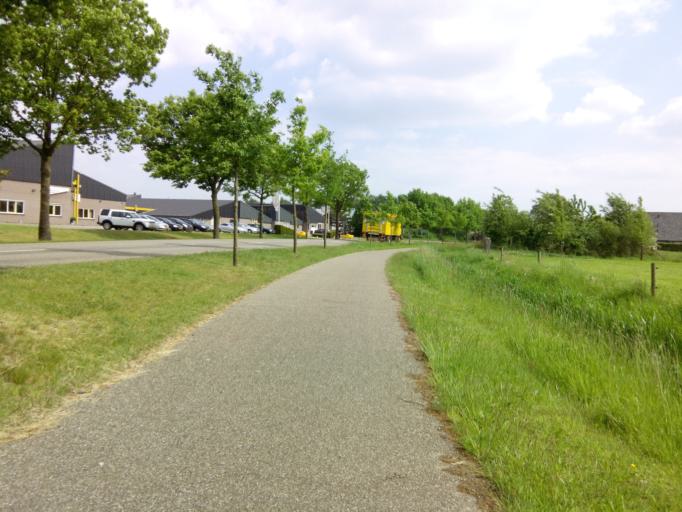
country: NL
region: Gelderland
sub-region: Berkelland
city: Borculo
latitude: 52.0618
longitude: 6.5693
